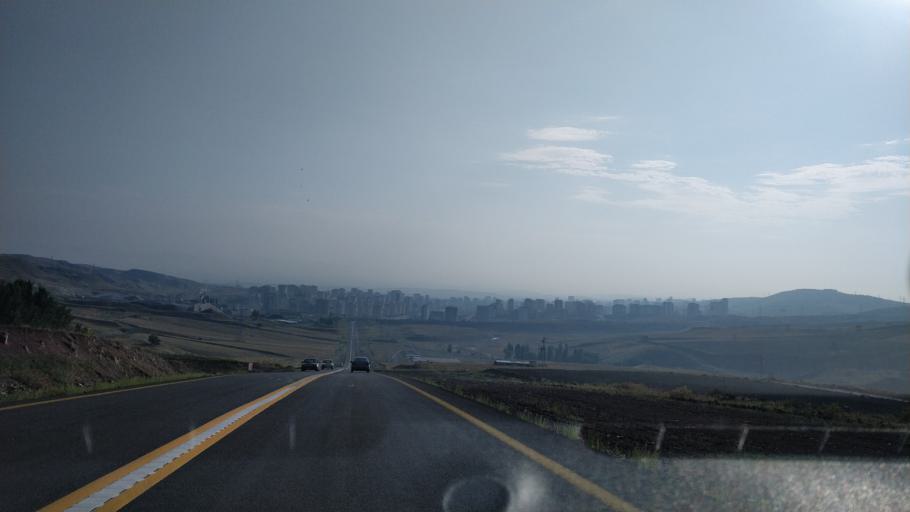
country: TR
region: Ankara
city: Etimesgut
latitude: 39.8756
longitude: 32.5982
